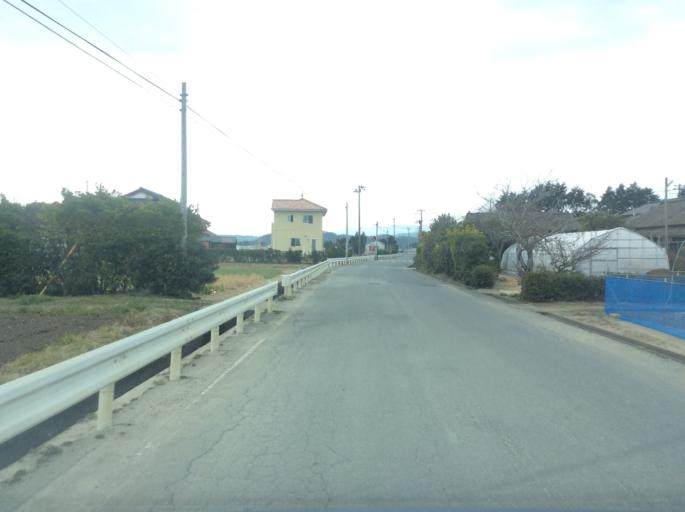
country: JP
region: Fukushima
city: Iwaki
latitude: 37.0810
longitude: 140.9712
